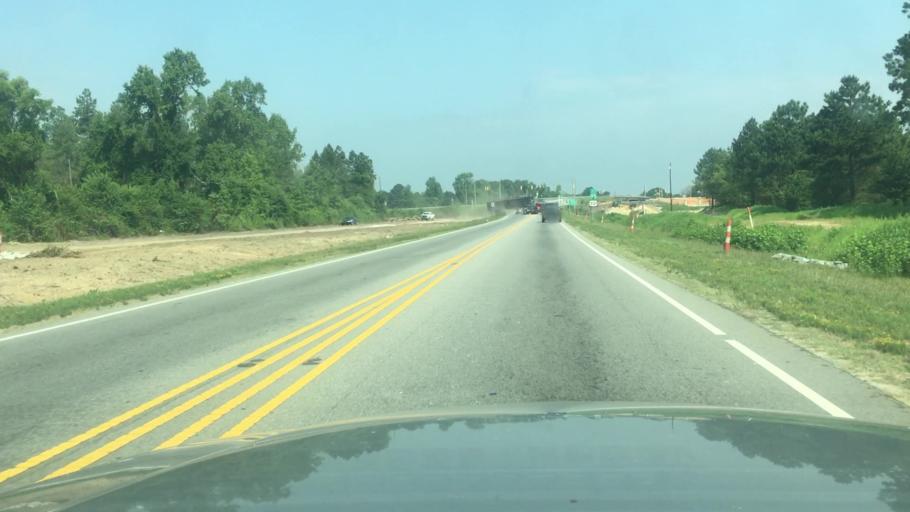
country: US
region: North Carolina
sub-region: Cumberland County
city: Hope Mills
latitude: 34.9423
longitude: -78.9273
